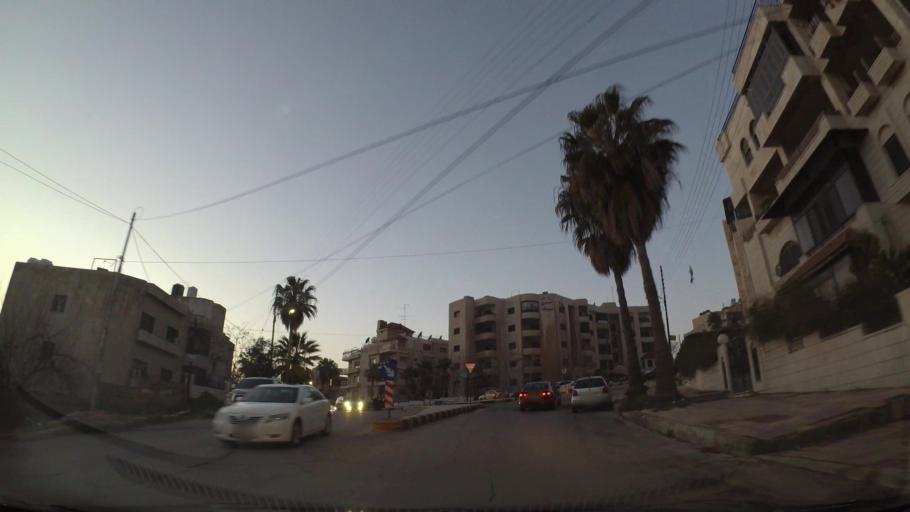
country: JO
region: Amman
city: Al Jubayhah
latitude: 31.9859
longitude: 35.8908
